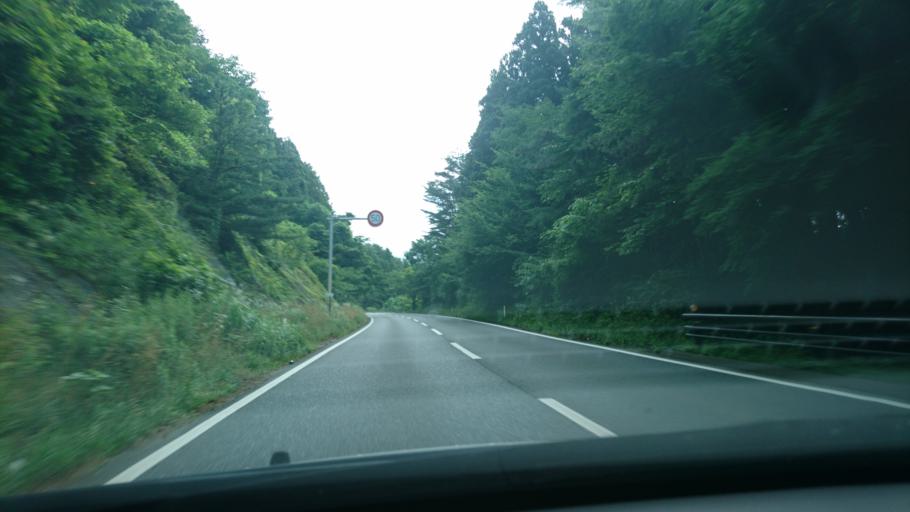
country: JP
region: Iwate
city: Kamaishi
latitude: 39.1597
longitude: 141.8471
